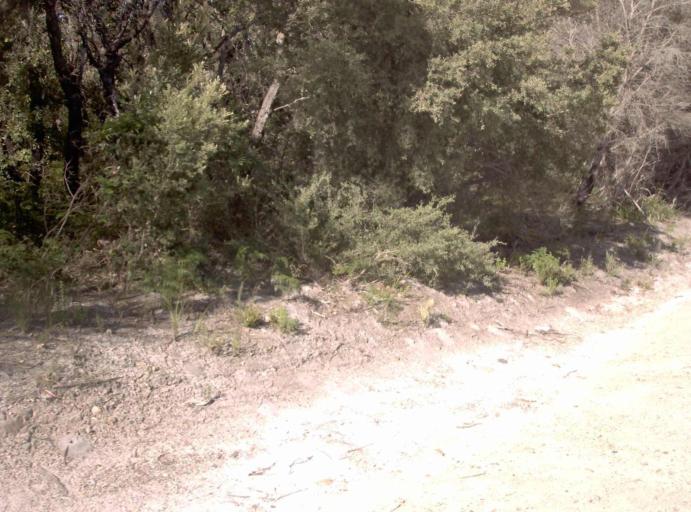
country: AU
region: Victoria
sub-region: East Gippsland
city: Lakes Entrance
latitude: -37.7970
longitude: 148.5477
